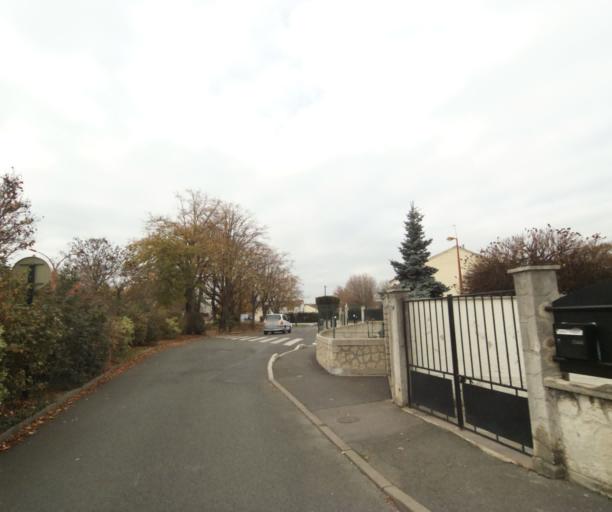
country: FR
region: Ile-de-France
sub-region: Departement du Val-d'Oise
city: Gonesse
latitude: 48.9838
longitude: 2.4376
